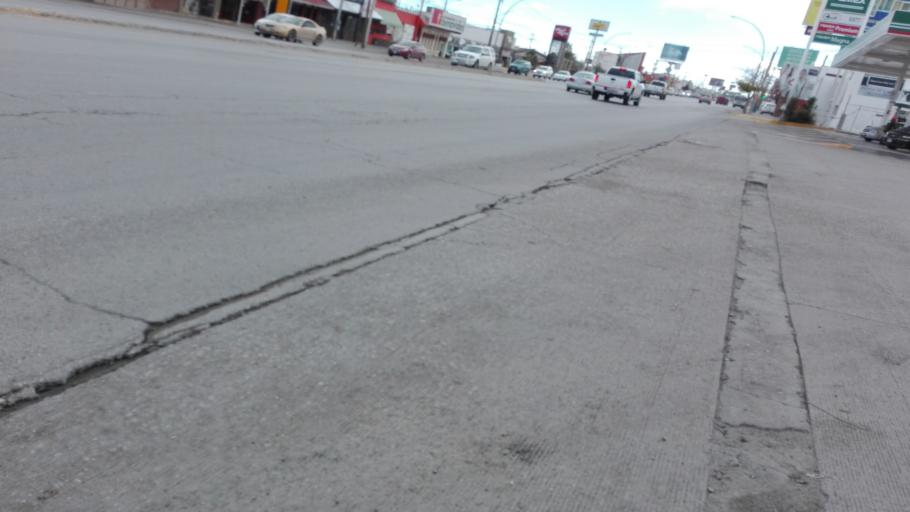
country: MX
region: Chihuahua
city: Ciudad Juarez
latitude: 31.7221
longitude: -106.4183
